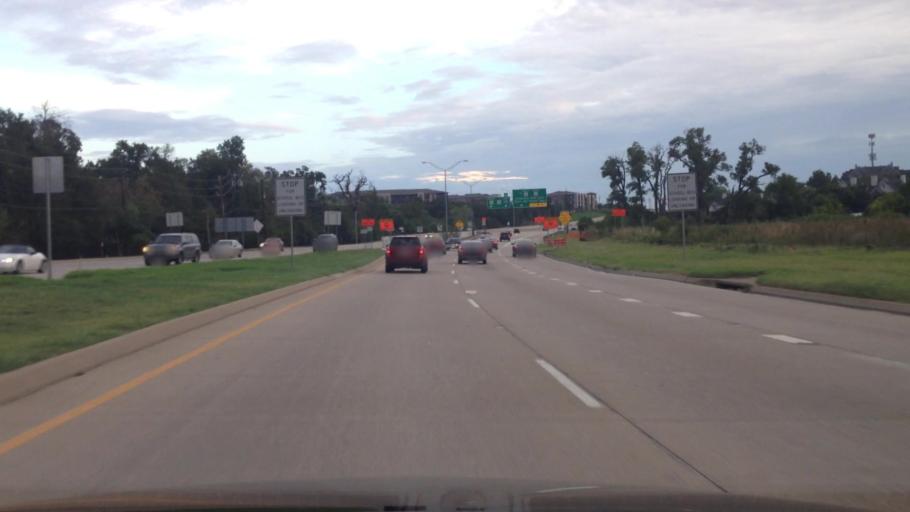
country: US
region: Texas
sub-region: Dallas County
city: Coppell
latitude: 32.9810
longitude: -97.0376
